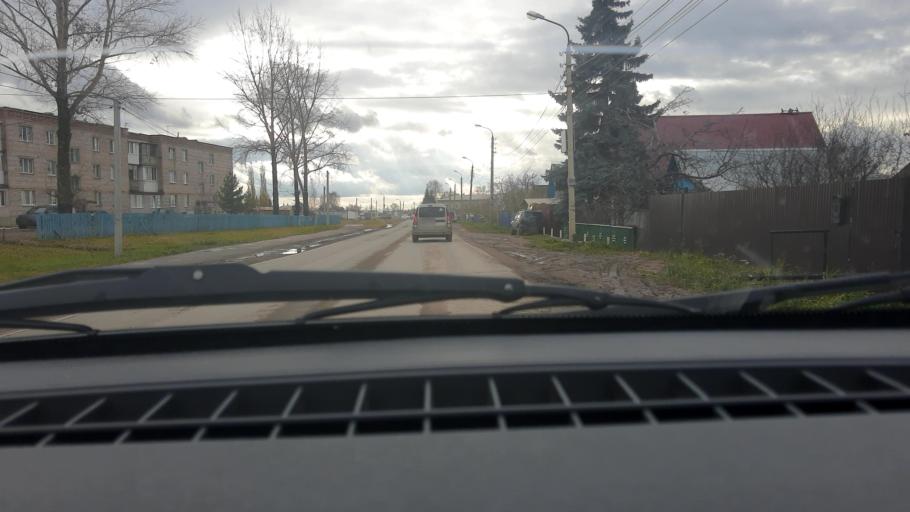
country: RU
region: Bashkortostan
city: Iglino
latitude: 54.7899
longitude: 56.2347
